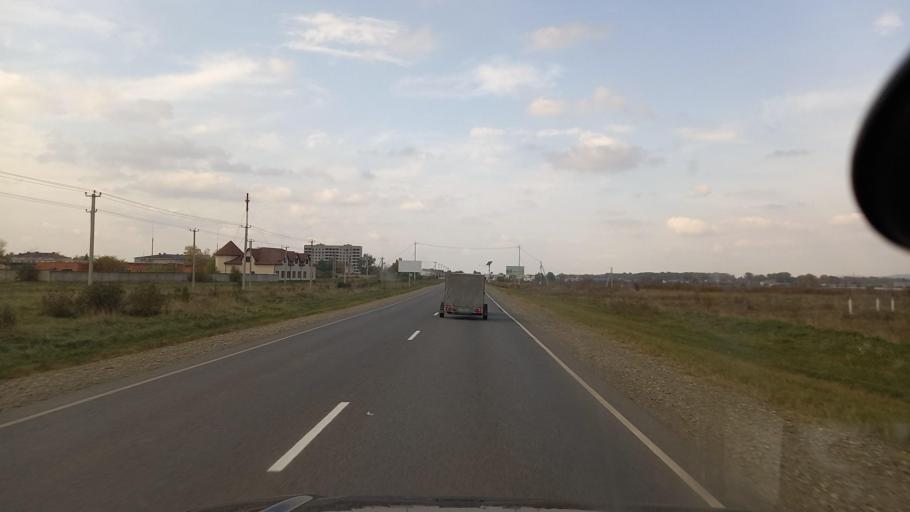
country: RU
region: Krasnodarskiy
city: Mostovskoy
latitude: 44.3874
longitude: 40.8174
